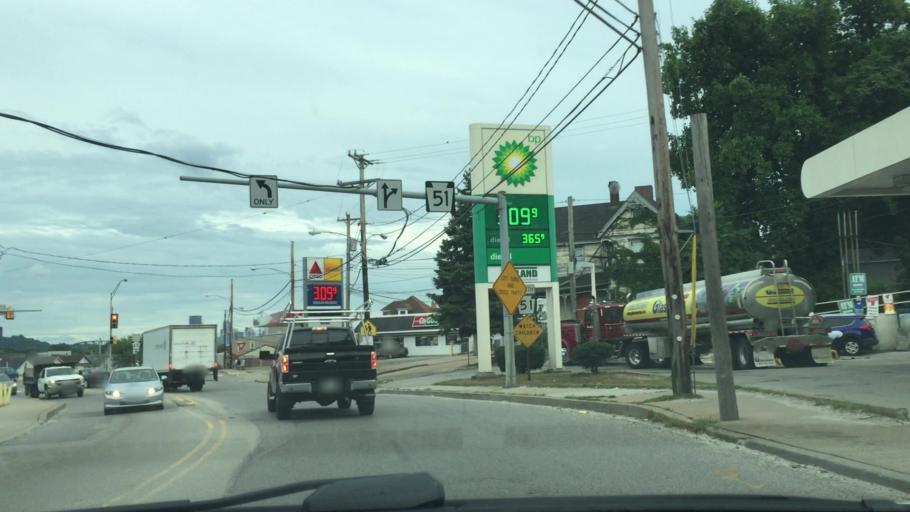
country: US
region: Pennsylvania
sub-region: Allegheny County
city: McKees Rocks
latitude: 40.4738
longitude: -80.0635
